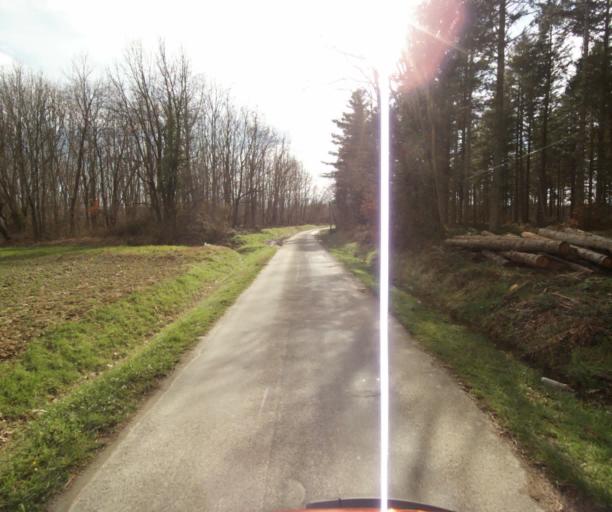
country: FR
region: Midi-Pyrenees
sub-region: Departement de l'Ariege
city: La Tour-du-Crieu
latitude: 43.0884
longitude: 1.7432
